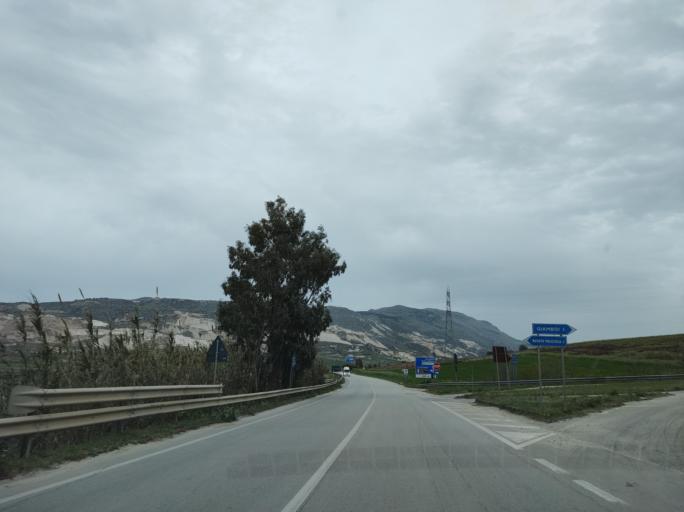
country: IT
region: Sicily
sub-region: Trapani
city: Custonaci
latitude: 38.0419
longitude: 12.6828
